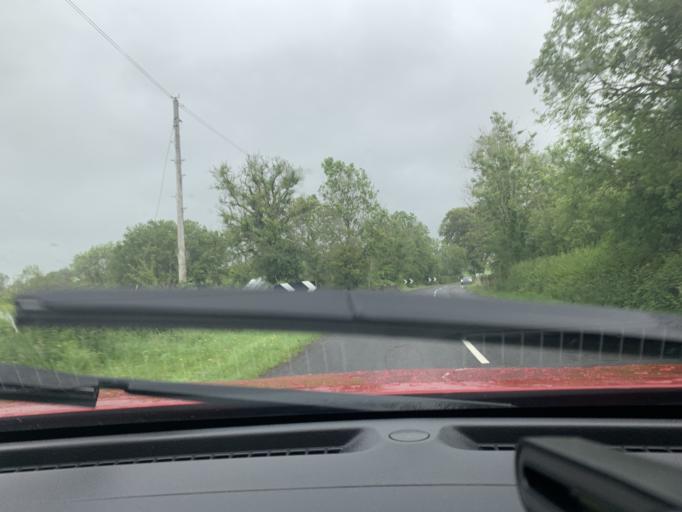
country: GB
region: Northern Ireland
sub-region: Fermanagh District
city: Enniskillen
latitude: 54.3079
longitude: -7.6861
